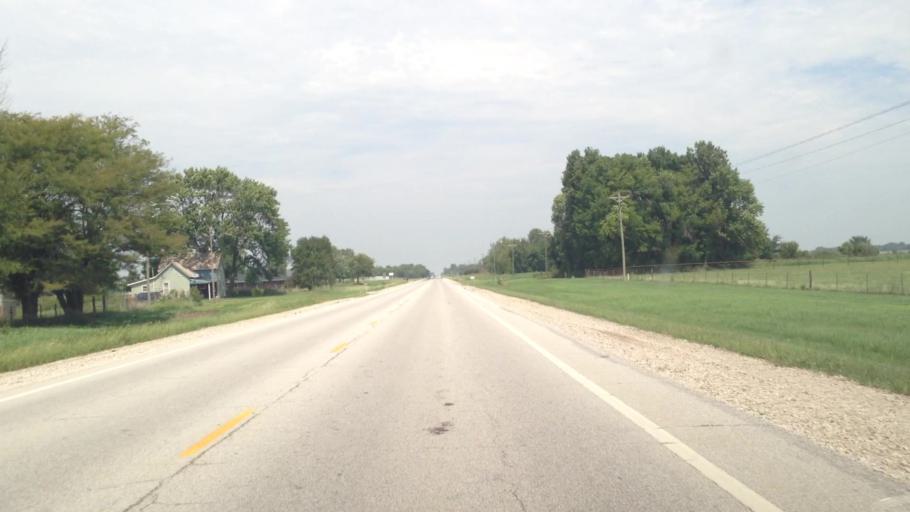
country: US
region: Kansas
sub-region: Neosho County
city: Erie
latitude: 37.5783
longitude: -95.2524
